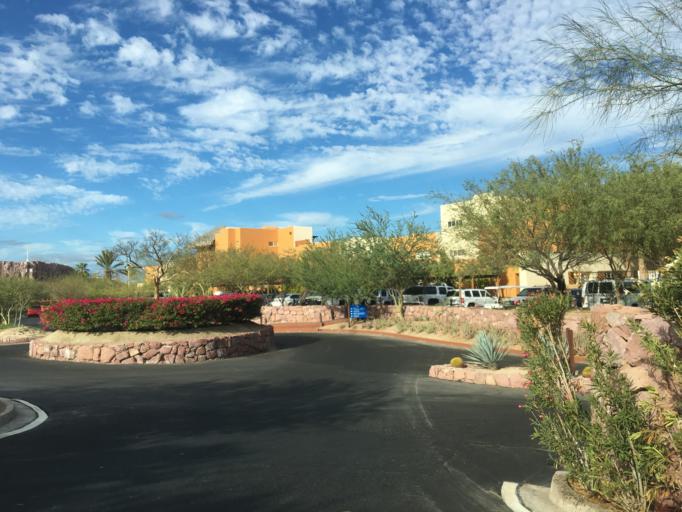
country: MX
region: Baja California Sur
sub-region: La Paz
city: La Paz
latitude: 24.2145
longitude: -110.2976
